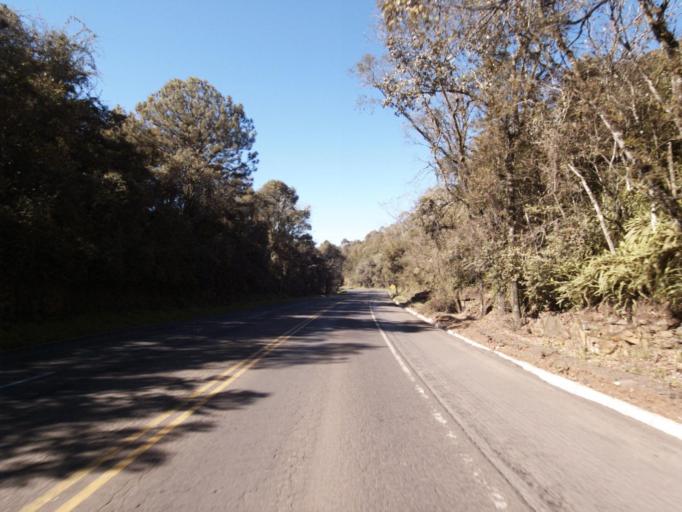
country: BR
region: Santa Catarina
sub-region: Sao Lourenco Do Oeste
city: Sao Lourenco dOeste
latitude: -26.8184
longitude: -53.1583
